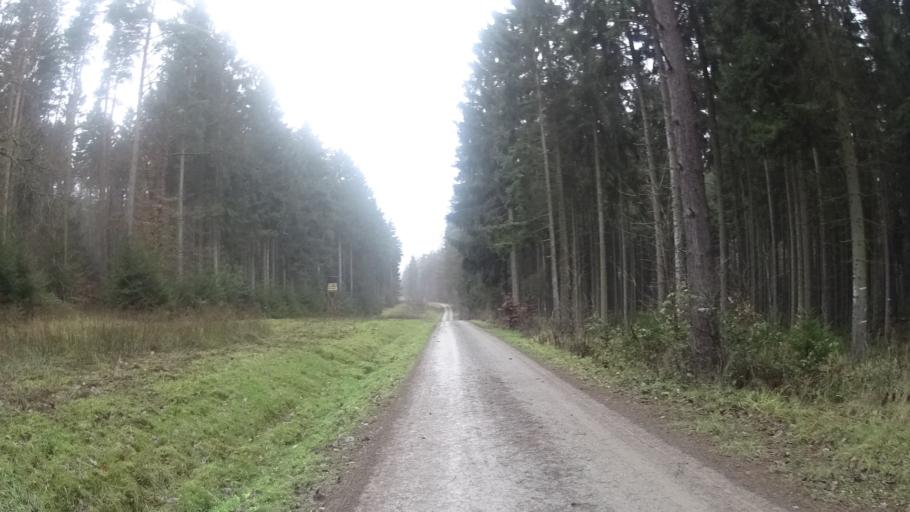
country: DE
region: Thuringia
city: Tissa
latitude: 50.8675
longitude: 11.7489
